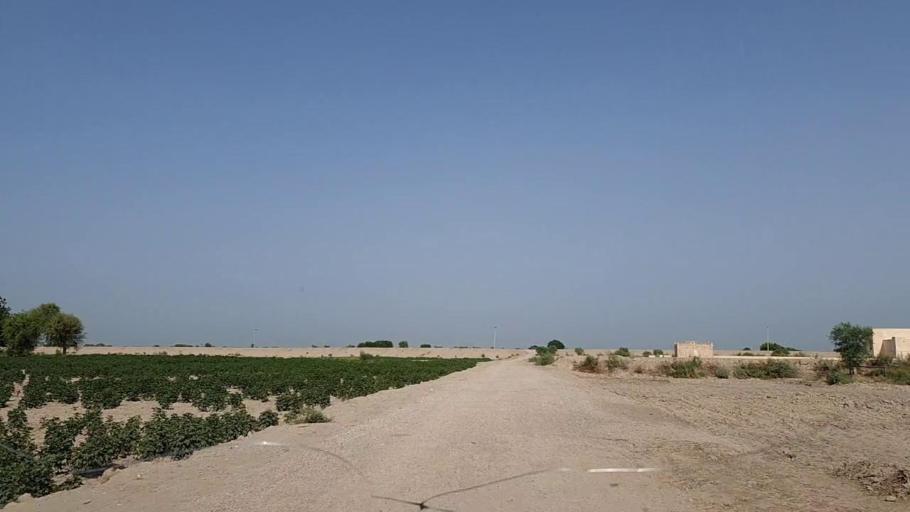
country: PK
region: Sindh
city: Kandiaro
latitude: 27.0729
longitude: 68.1399
